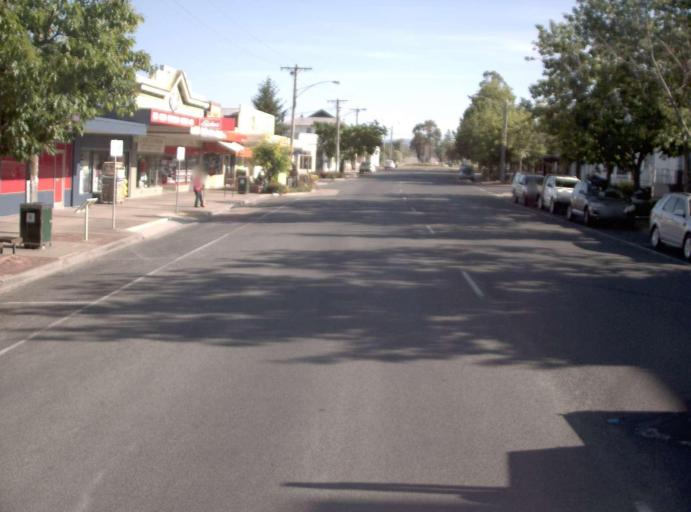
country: AU
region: Victoria
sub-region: East Gippsland
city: Lakes Entrance
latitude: -37.7065
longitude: 148.4551
